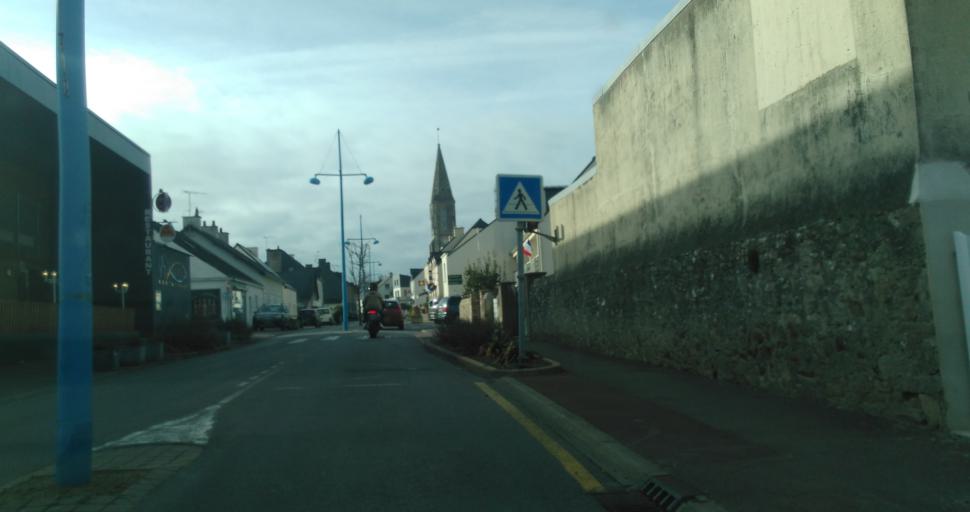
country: FR
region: Brittany
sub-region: Departement du Morbihan
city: Penestin
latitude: 47.4831
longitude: -2.4707
